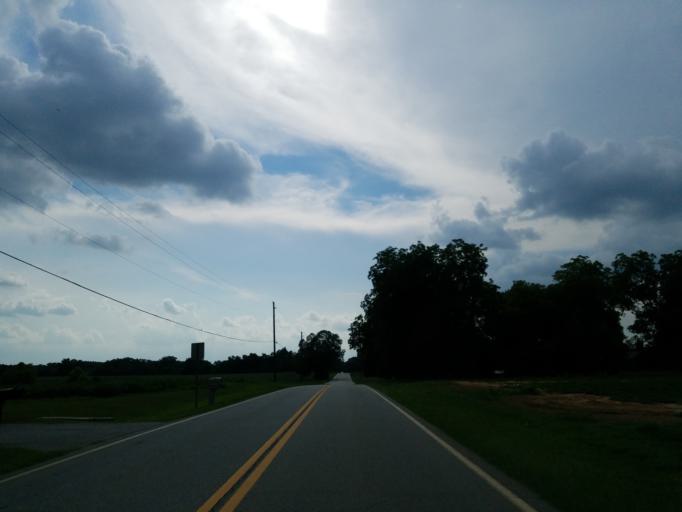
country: US
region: Georgia
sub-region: Dooly County
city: Unadilla
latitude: 32.2604
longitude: -83.7211
